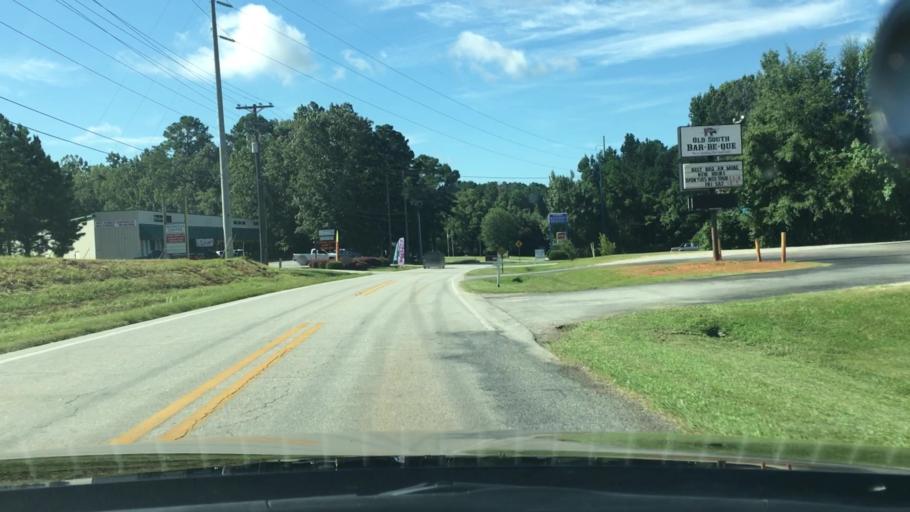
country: US
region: Georgia
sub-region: Putnam County
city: Jefferson
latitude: 33.4186
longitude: -83.2672
